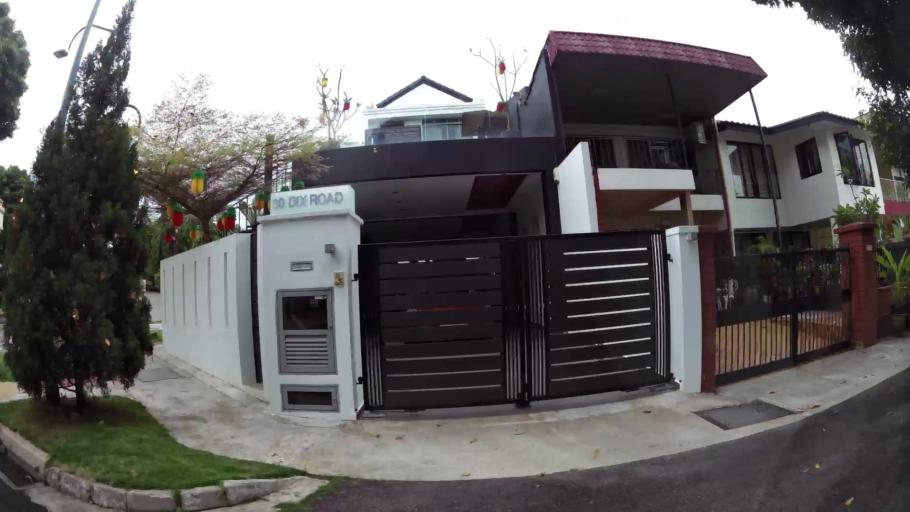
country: SG
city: Singapore
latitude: 1.3613
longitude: 103.8770
